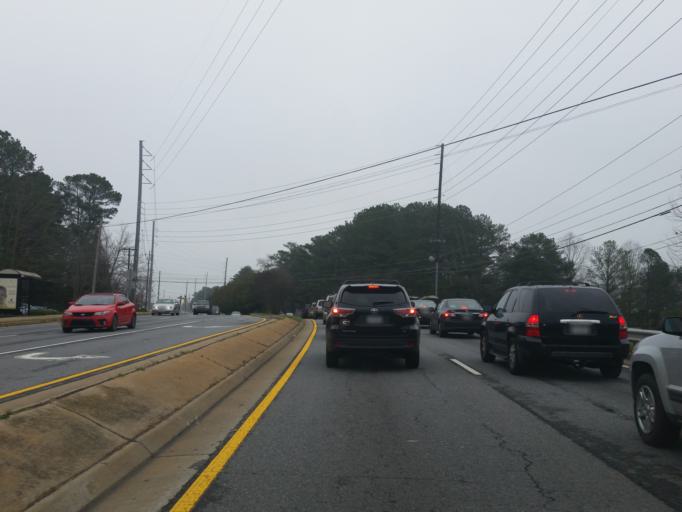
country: US
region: Georgia
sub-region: Fulton County
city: Sandy Springs
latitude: 33.9782
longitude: -84.4365
